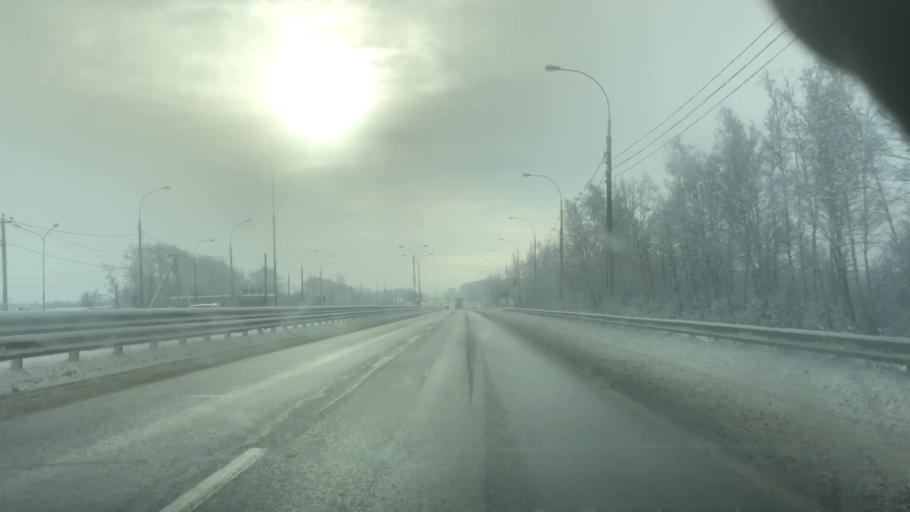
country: RU
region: Tula
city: Venev
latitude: 54.3447
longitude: 38.1546
